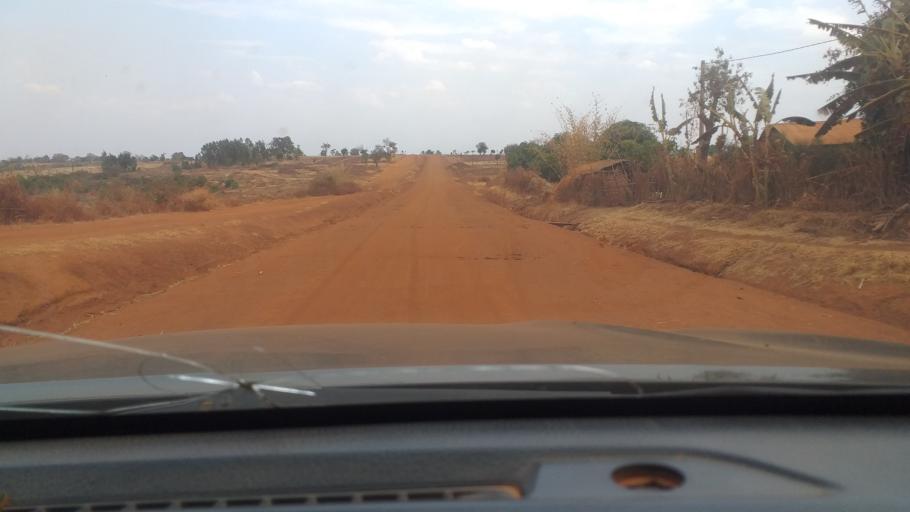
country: ET
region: Binshangul Gumuz
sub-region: Asosa
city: Asosa
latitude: 10.0660
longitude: 34.6809
